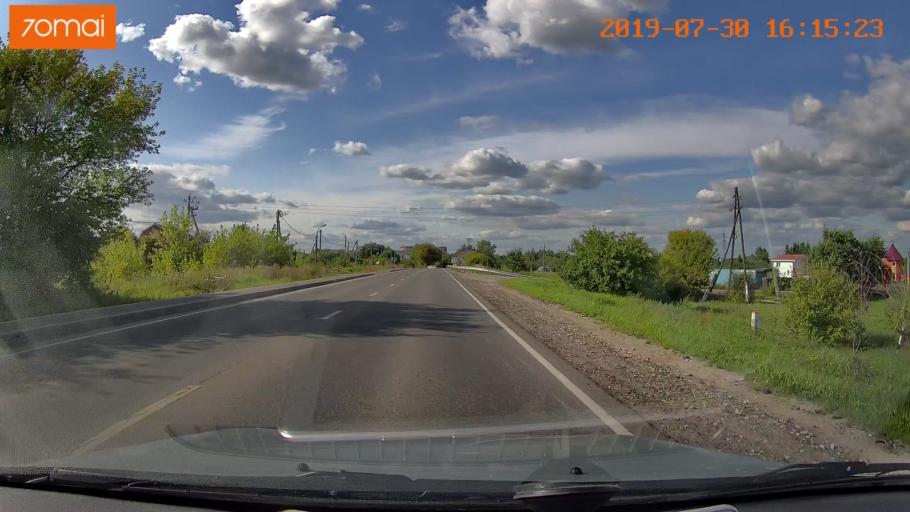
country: RU
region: Moskovskaya
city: Voskresensk
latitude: 55.2957
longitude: 38.6679
